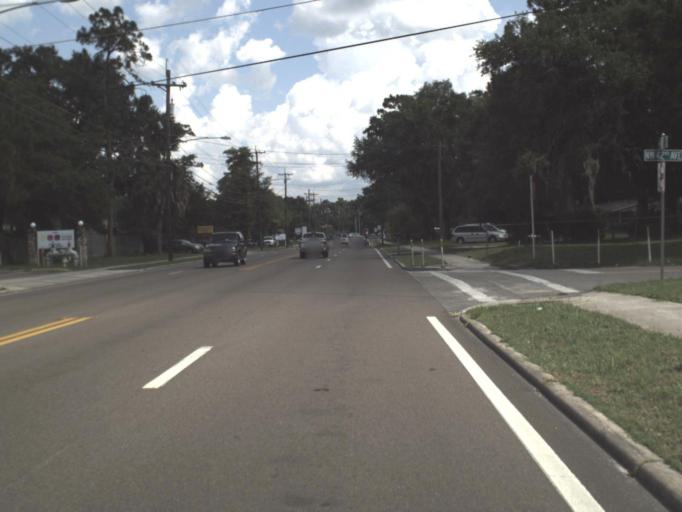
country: US
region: Florida
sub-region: Alachua County
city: Gainesville
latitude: 29.6924
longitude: -82.3332
